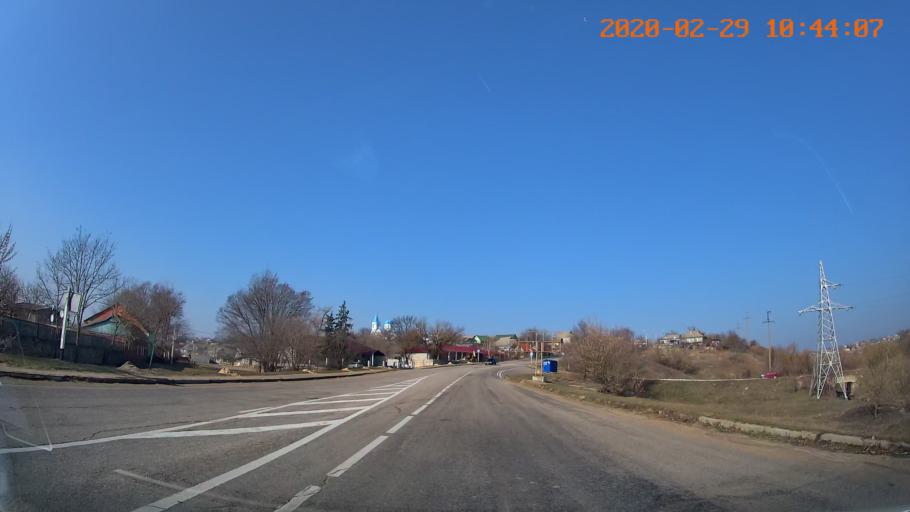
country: MD
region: Telenesti
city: Grigoriopol
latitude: 47.0679
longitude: 29.3986
